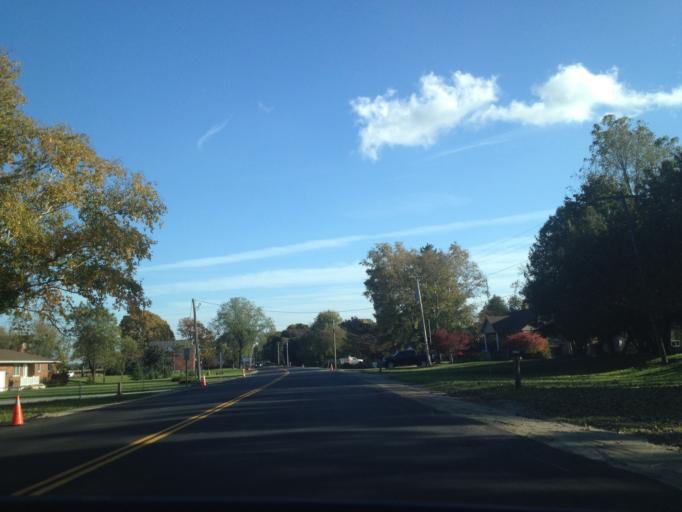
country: CA
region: Ontario
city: Delaware
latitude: 42.5956
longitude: -81.5965
